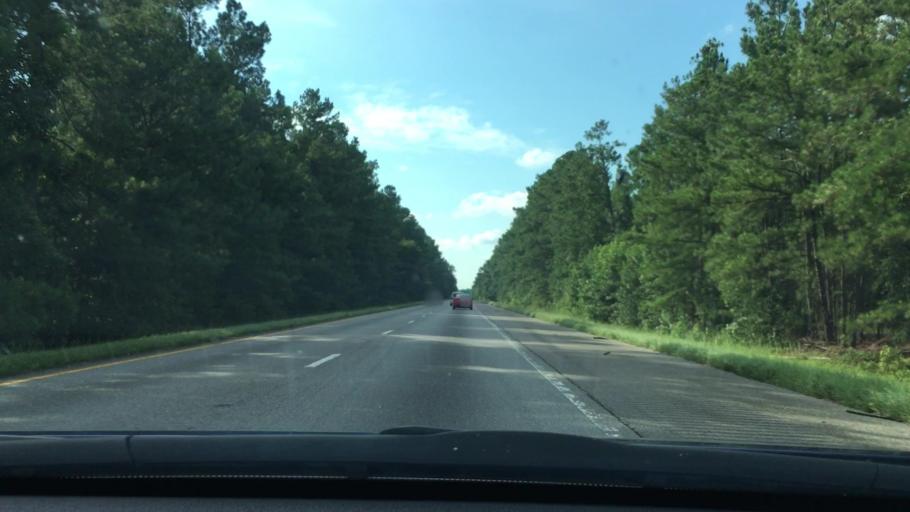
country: US
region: South Carolina
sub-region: Orangeburg County
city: Holly Hill
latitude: 33.3074
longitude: -80.5370
